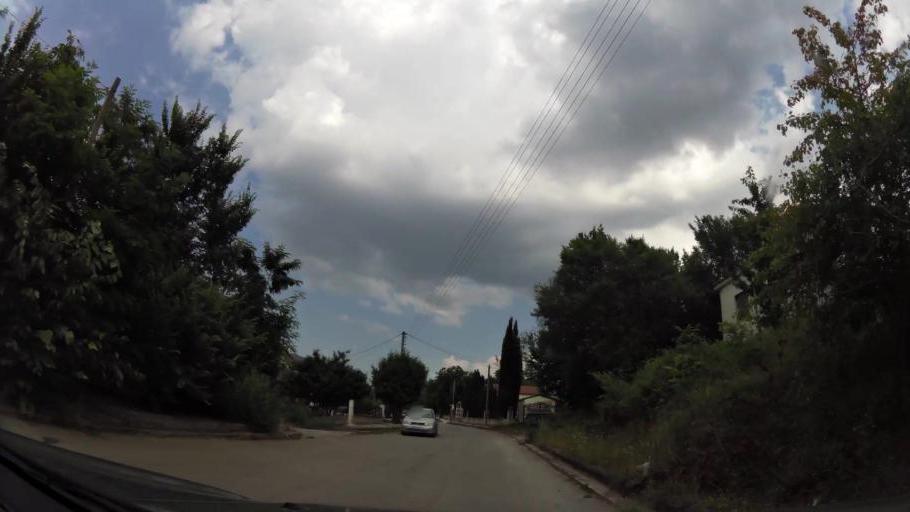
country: GR
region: West Macedonia
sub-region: Nomos Kozanis
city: Koila
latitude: 40.3490
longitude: 21.8343
